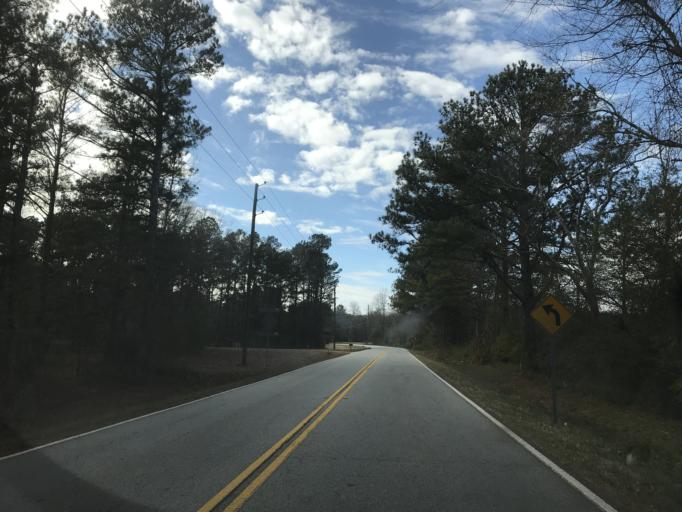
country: US
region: Georgia
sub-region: Douglas County
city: Douglasville
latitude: 33.7963
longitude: -84.7684
